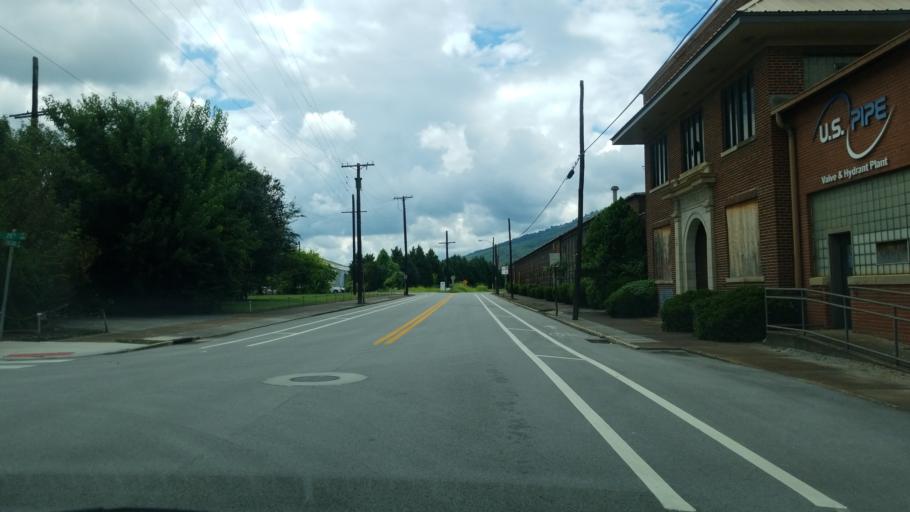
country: US
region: Tennessee
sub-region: Hamilton County
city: Chattanooga
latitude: 35.0294
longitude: -85.3184
